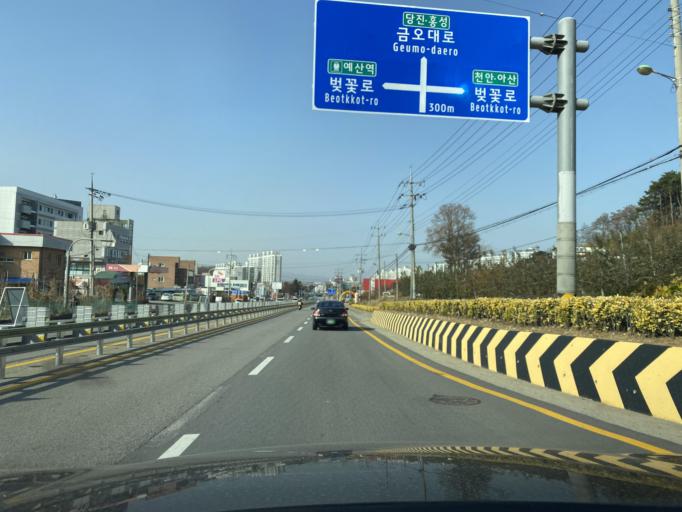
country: KR
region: Chungcheongnam-do
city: Yesan
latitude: 36.6911
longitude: 126.8402
